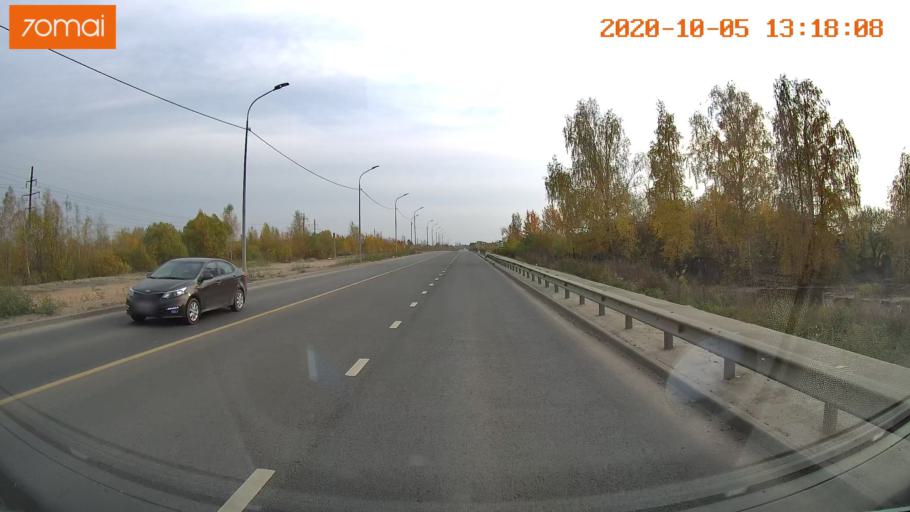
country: RU
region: Ivanovo
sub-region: Gorod Ivanovo
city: Ivanovo
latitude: 56.9800
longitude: 40.9170
